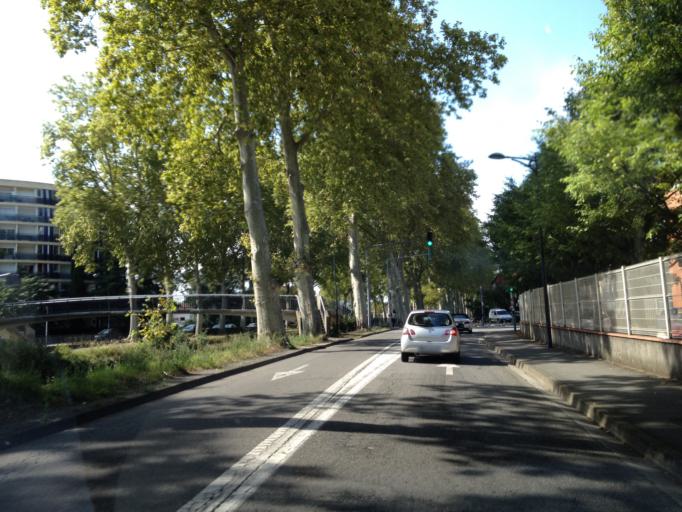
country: FR
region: Midi-Pyrenees
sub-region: Departement de la Haute-Garonne
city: Toulouse
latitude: 43.5815
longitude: 1.4634
